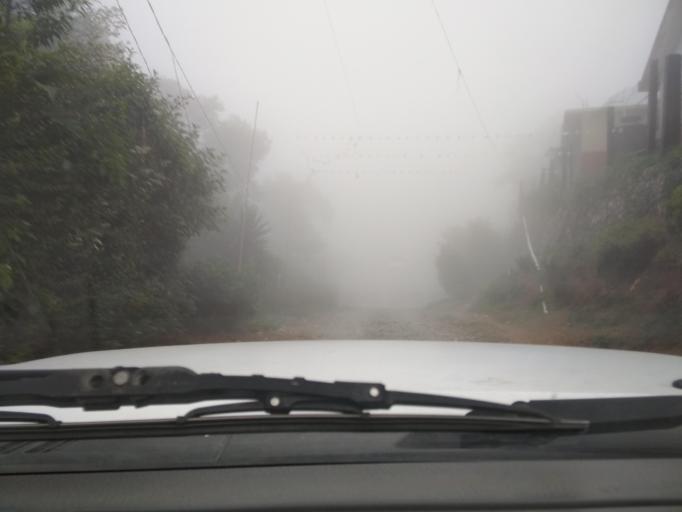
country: MX
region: Veracruz
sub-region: La Perla
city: Barrio de San Miguel
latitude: 18.9413
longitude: -97.1180
